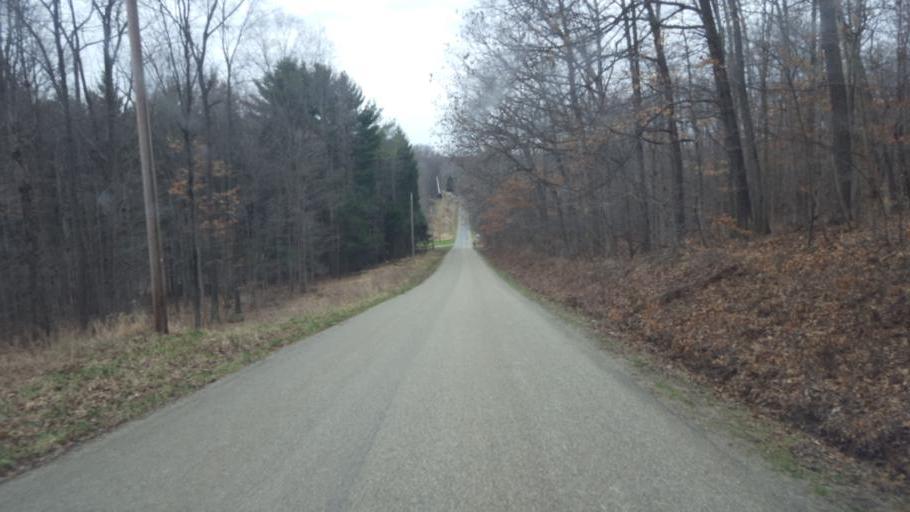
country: US
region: Ohio
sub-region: Sandusky County
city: Bellville
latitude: 40.5727
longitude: -82.3882
